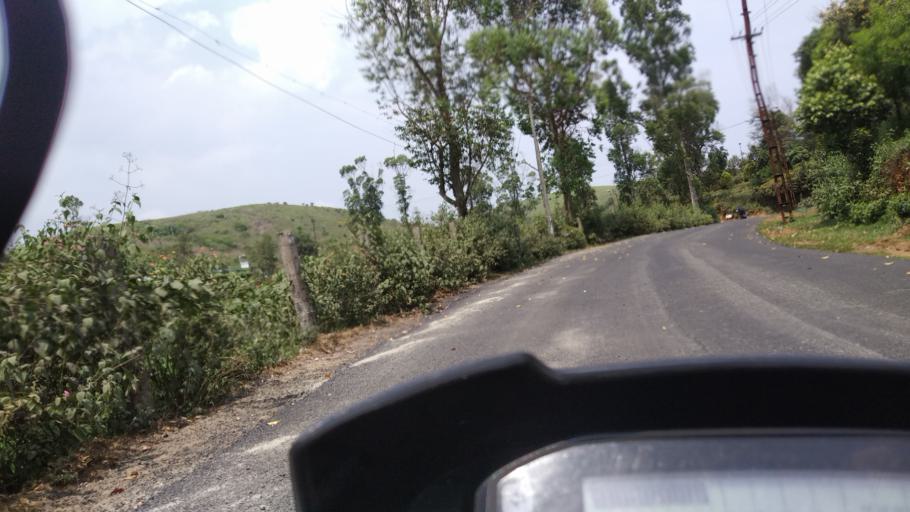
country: IN
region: Kerala
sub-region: Kottayam
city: Erattupetta
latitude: 9.6509
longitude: 76.9269
